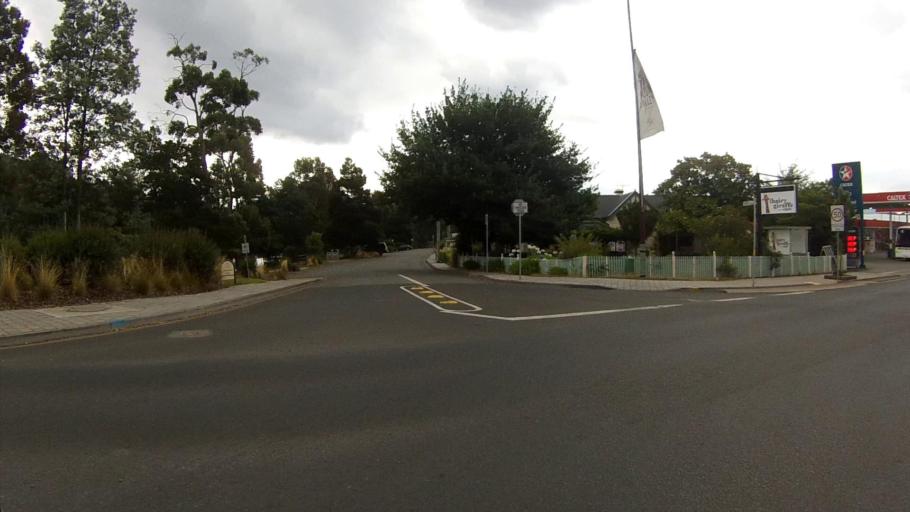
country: AU
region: Tasmania
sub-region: Huon Valley
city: Huonville
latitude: -43.0331
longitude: 147.0471
